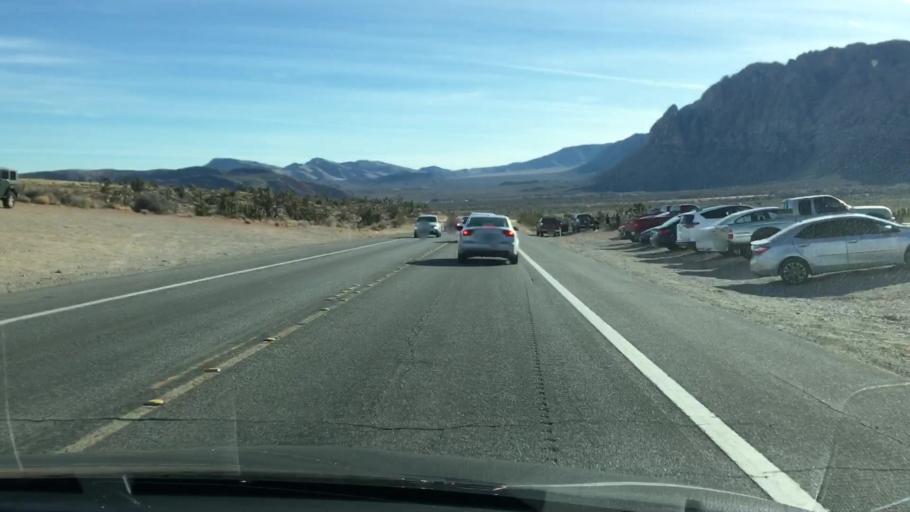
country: US
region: Nevada
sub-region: Clark County
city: Summerlin South
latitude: 36.0899
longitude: -115.4493
